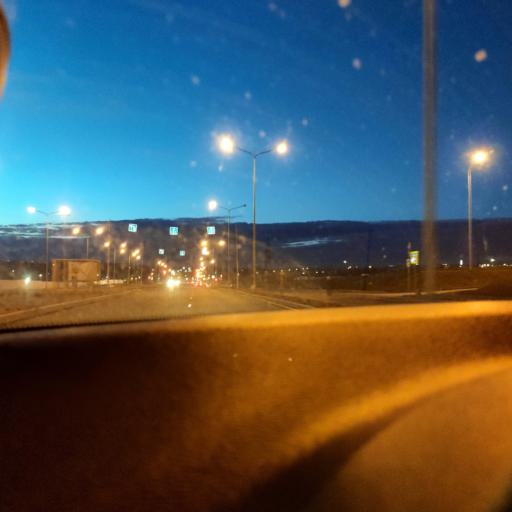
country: RU
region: Samara
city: Petra-Dubrava
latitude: 53.2969
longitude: 50.3231
